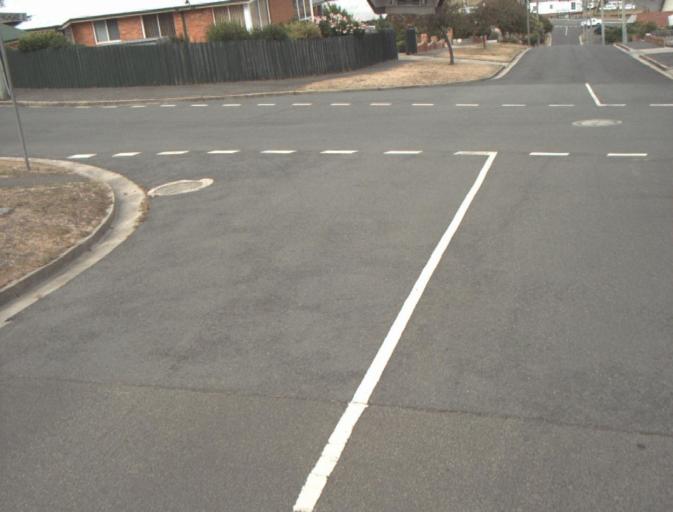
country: AU
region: Tasmania
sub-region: Launceston
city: Summerhill
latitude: -41.4787
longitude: 147.1690
